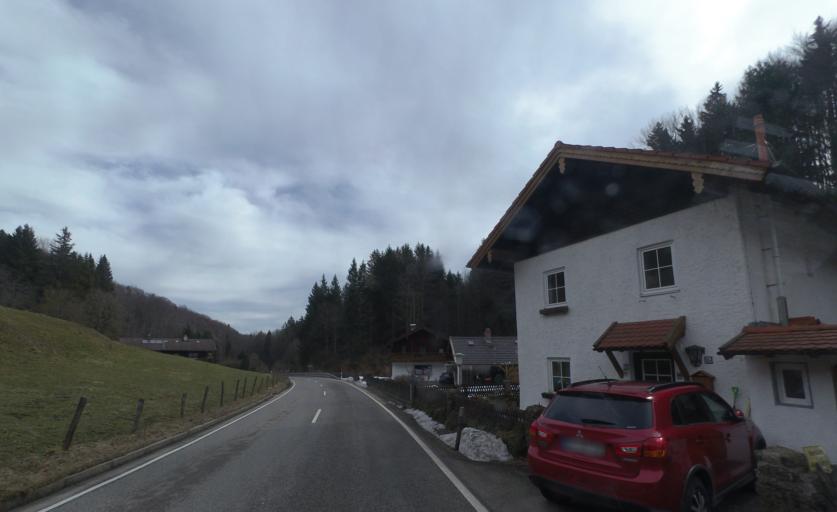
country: DE
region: Bavaria
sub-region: Upper Bavaria
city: Teisendorf
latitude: 47.8320
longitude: 12.7608
